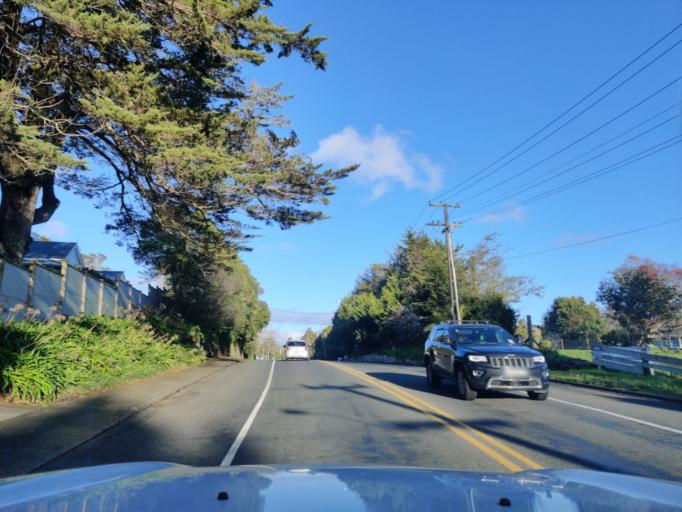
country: NZ
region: Auckland
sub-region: Auckland
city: Pakuranga
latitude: -36.9476
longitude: 174.9640
